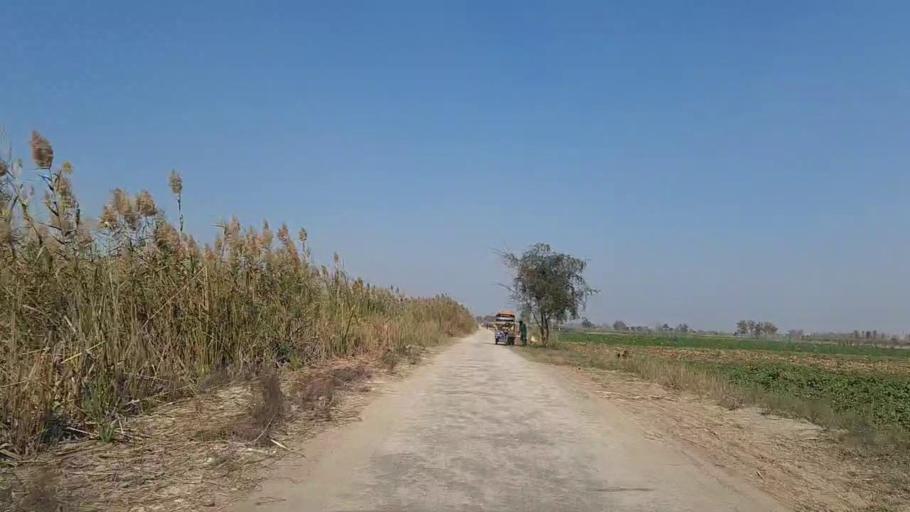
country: PK
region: Sindh
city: Daur
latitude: 26.5040
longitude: 68.3464
